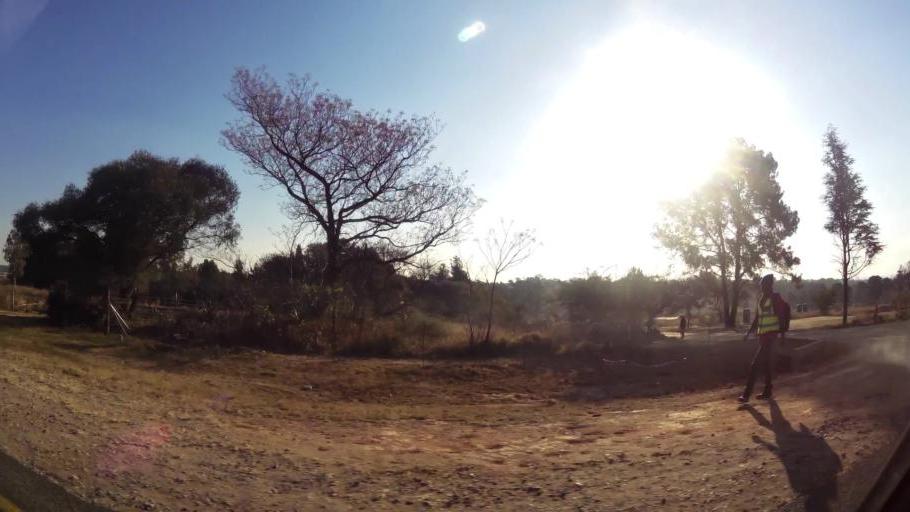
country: ZA
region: Gauteng
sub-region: West Rand District Municipality
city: Muldersdriseloop
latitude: -26.0191
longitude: 27.9090
